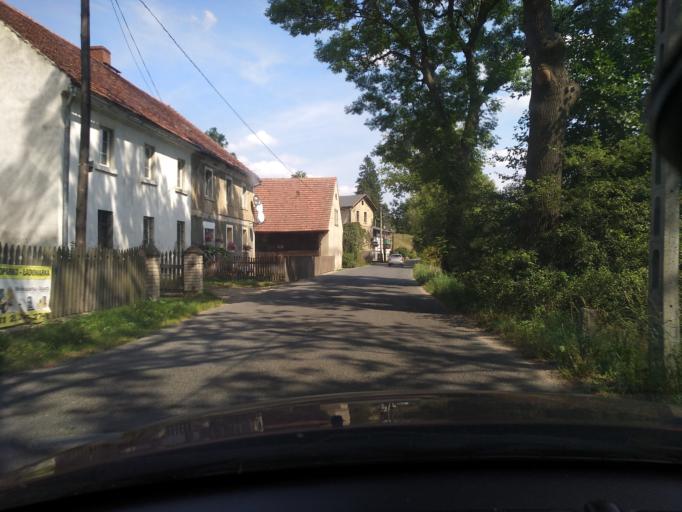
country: PL
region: Lower Silesian Voivodeship
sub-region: Powiat jeleniogorski
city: Stara Kamienica
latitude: 50.9369
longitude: 15.5906
